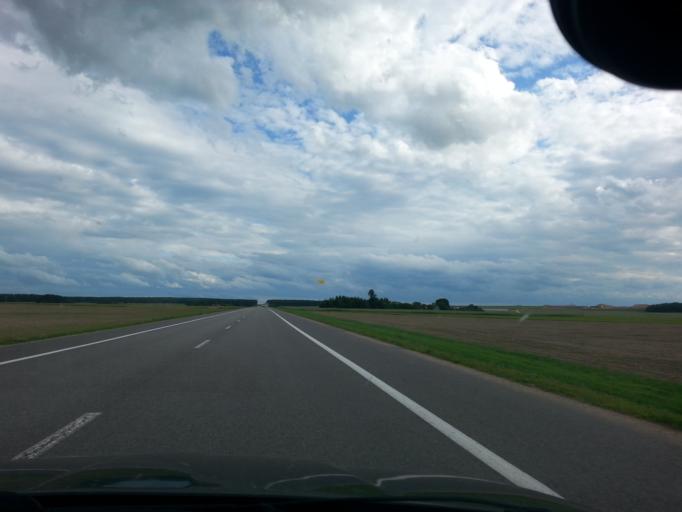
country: BY
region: Grodnenskaya
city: Astravyets
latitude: 54.7262
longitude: 26.0852
